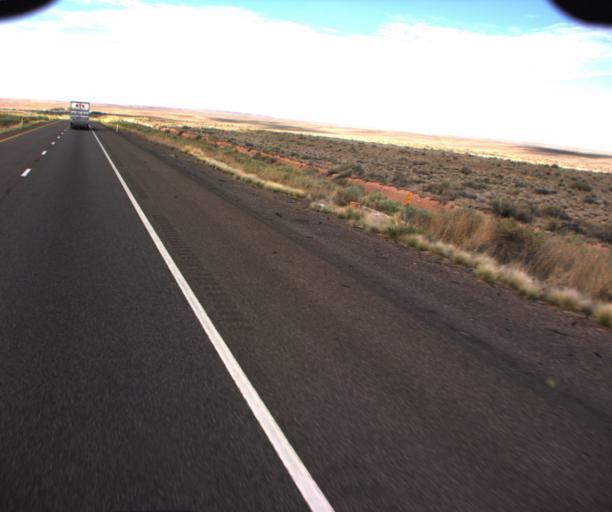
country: US
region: Arizona
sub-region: Navajo County
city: Holbrook
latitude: 35.0912
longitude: -109.6853
